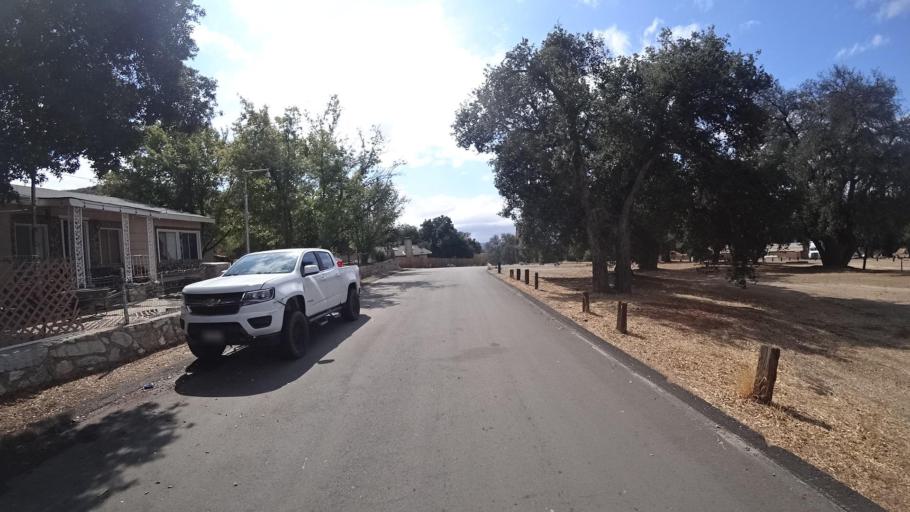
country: US
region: California
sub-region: San Diego County
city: Campo
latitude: 32.6890
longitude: -116.3340
